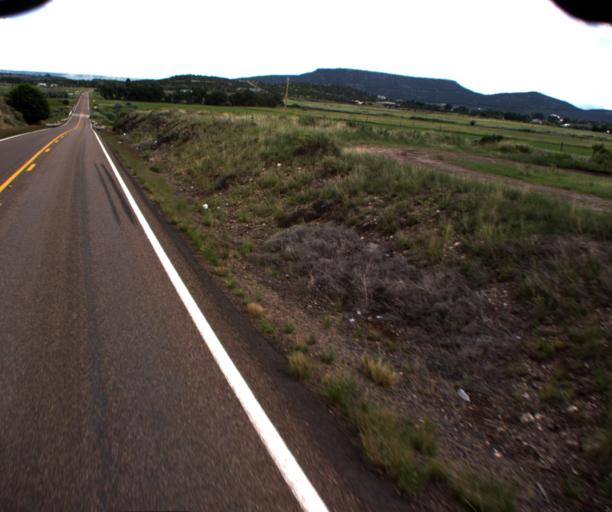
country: US
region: Arizona
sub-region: Apache County
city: Eagar
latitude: 34.1108
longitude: -109.3184
